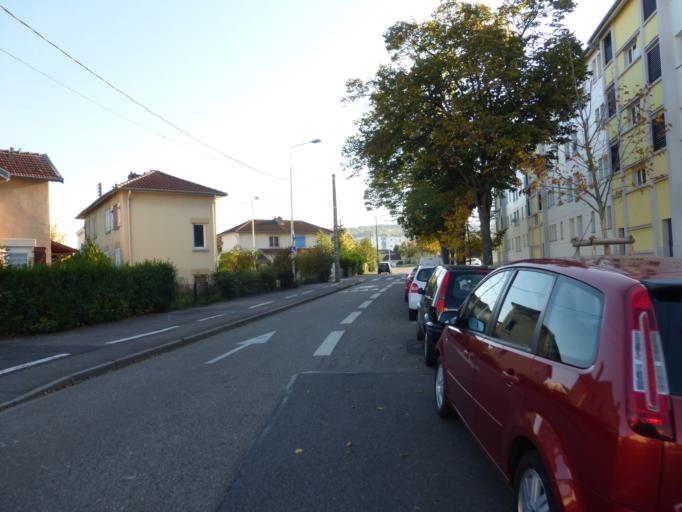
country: FR
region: Lorraine
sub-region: Departement de Meurthe-et-Moselle
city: Villers-les-Nancy
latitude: 48.6705
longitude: 6.1643
